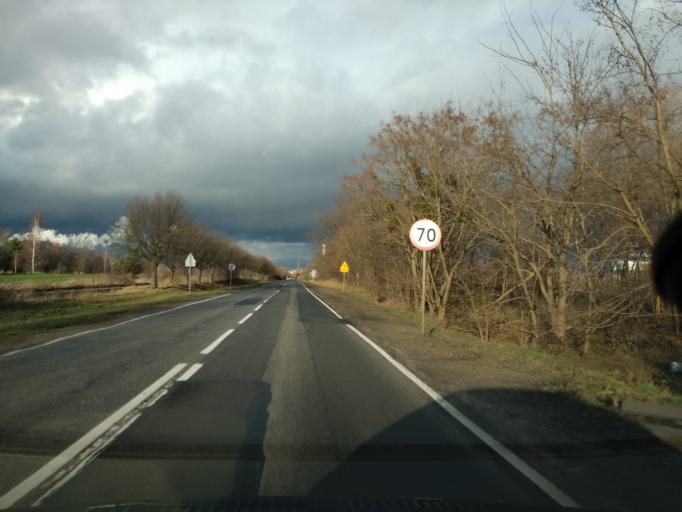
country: PL
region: Greater Poland Voivodeship
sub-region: Konin
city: Konin
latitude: 52.2696
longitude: 18.2670
